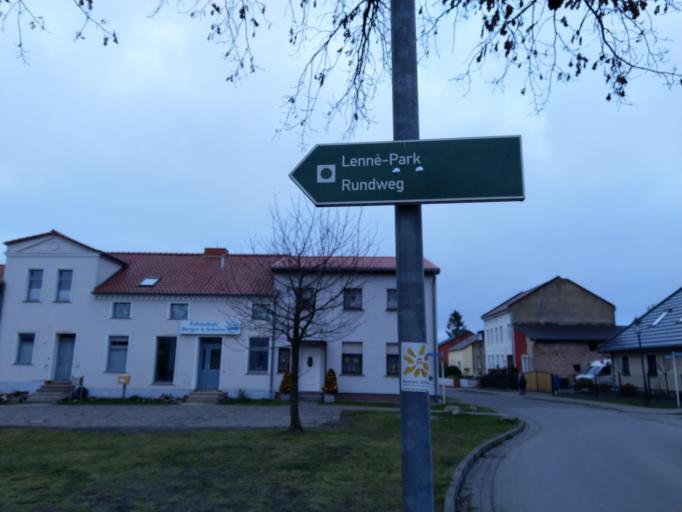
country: DE
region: Brandenburg
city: Ahrensfelde
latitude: 52.6024
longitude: 13.6165
